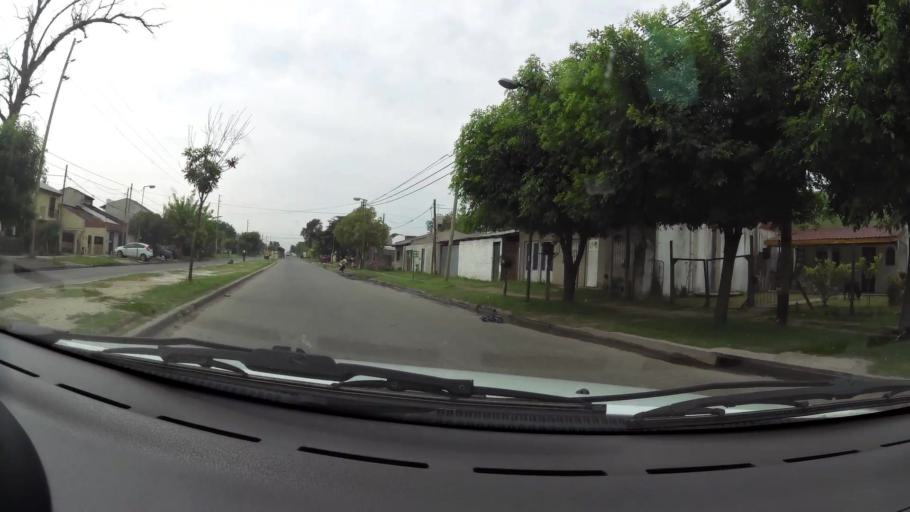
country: AR
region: Buenos Aires
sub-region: Partido de La Plata
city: La Plata
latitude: -34.9331
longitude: -58.0086
